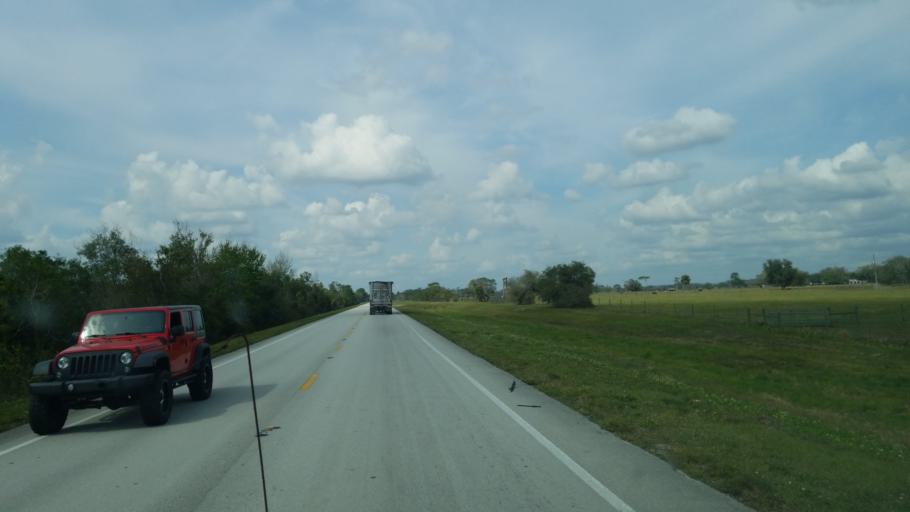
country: US
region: Florida
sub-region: Indian River County
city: Fellsmere
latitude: 27.7086
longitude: -80.9089
